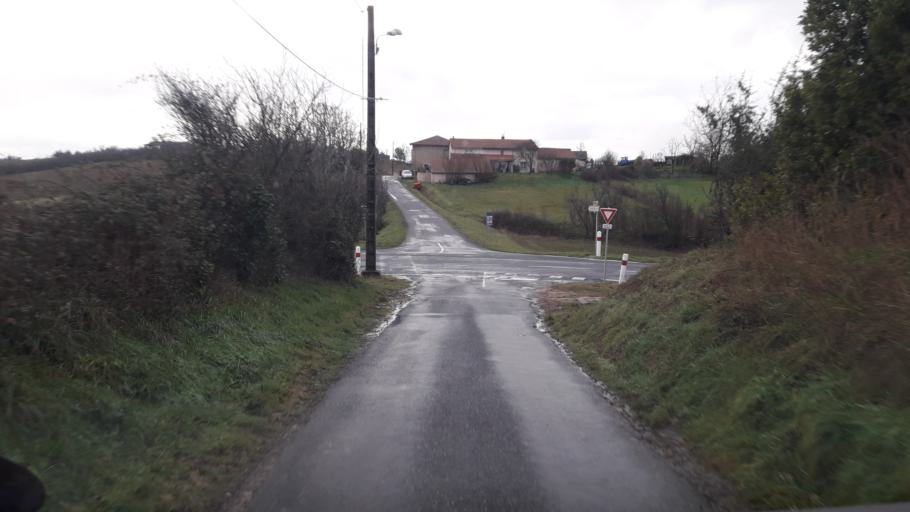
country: FR
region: Midi-Pyrenees
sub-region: Departement de la Haute-Garonne
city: Carbonne
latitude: 43.2872
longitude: 1.2454
